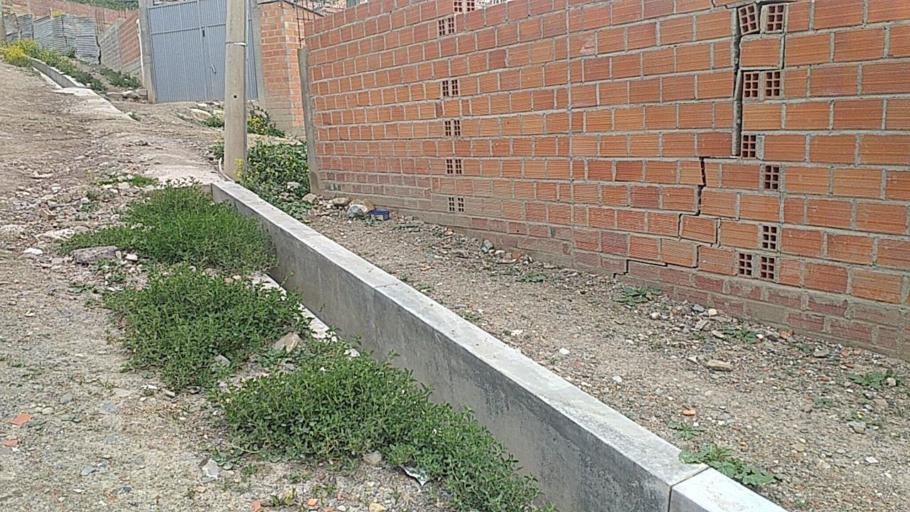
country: BO
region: La Paz
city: La Paz
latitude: -16.5374
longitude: -68.1390
